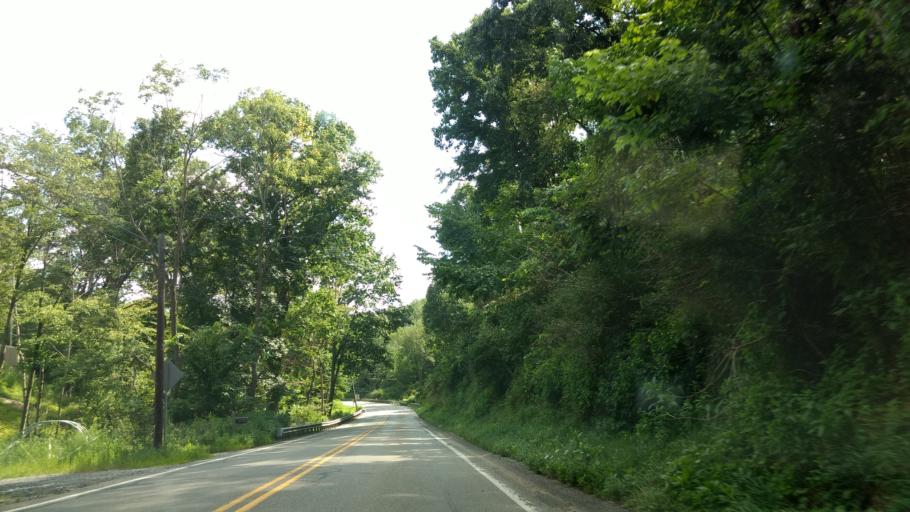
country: US
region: Pennsylvania
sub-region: Allegheny County
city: Franklin Park
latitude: 40.6061
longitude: -80.1164
